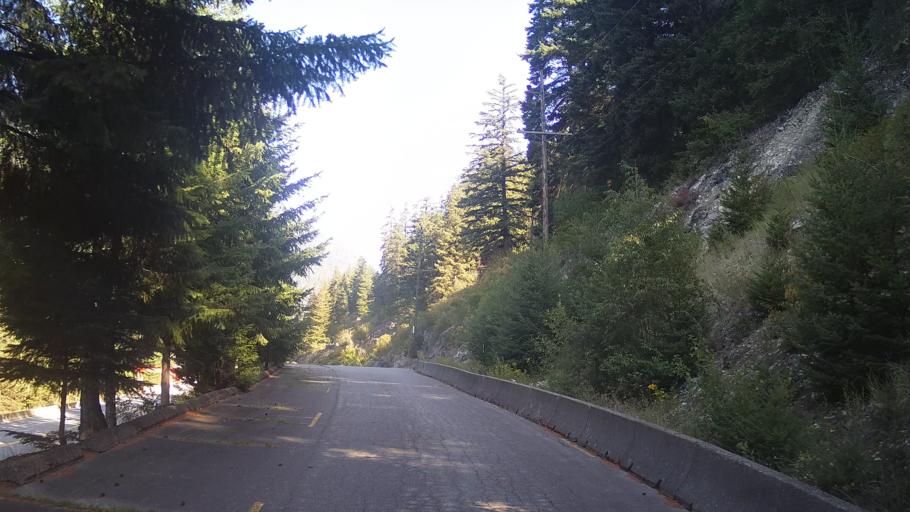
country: CA
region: British Columbia
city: Hope
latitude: 49.7793
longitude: -121.4432
